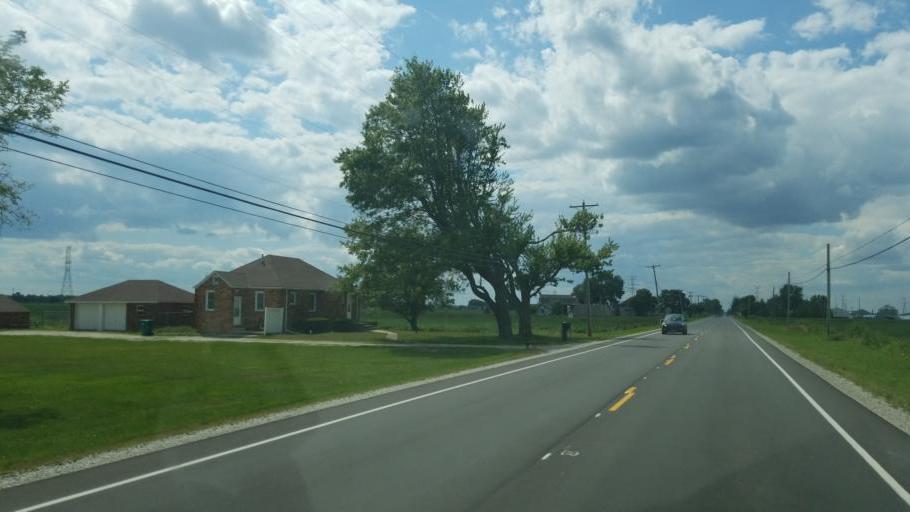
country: US
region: Ohio
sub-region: Lucas County
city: Curtice
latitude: 41.6386
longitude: -83.3217
